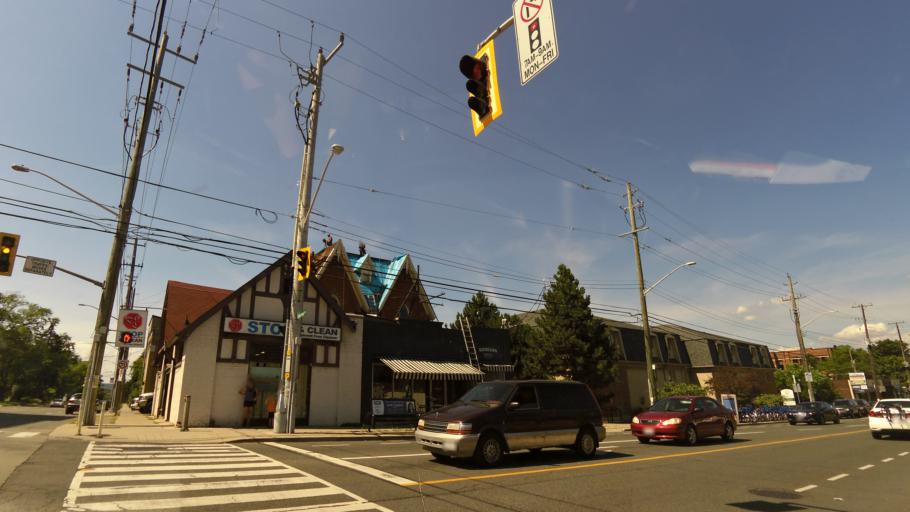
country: CA
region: Ontario
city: Hamilton
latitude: 43.2503
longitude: -79.8929
